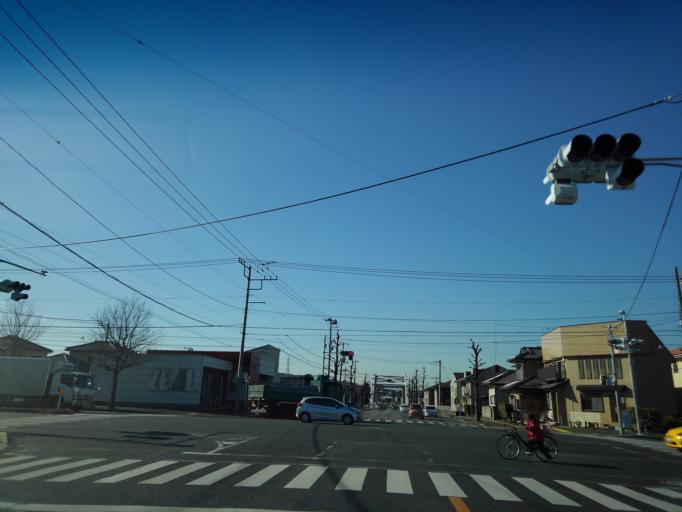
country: JP
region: Chiba
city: Kimitsu
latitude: 35.3244
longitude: 139.9104
